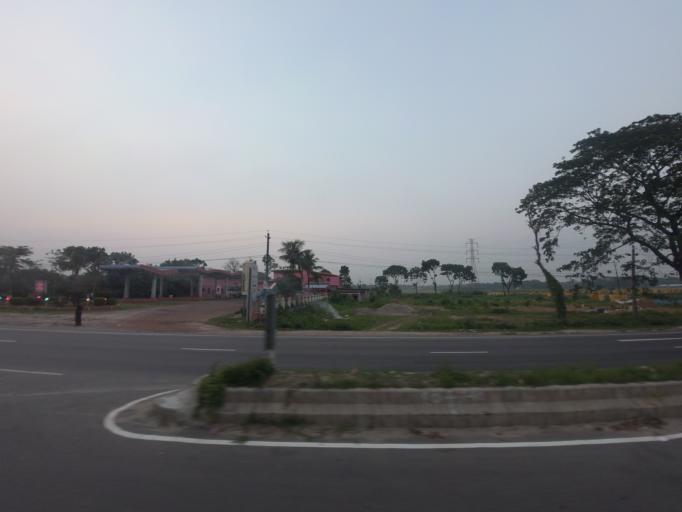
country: BD
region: Chittagong
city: Comilla
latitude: 23.4775
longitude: 91.1004
